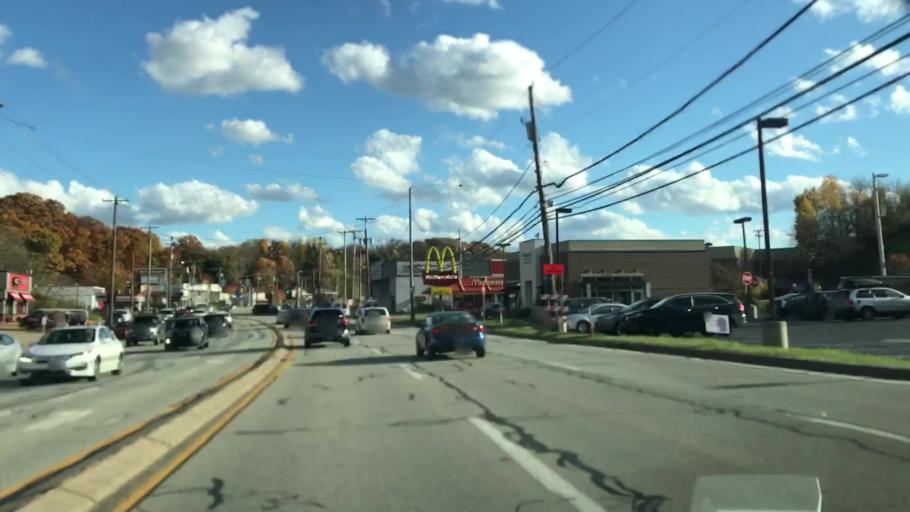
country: US
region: Pennsylvania
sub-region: Allegheny County
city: West View
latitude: 40.5297
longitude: -80.0091
